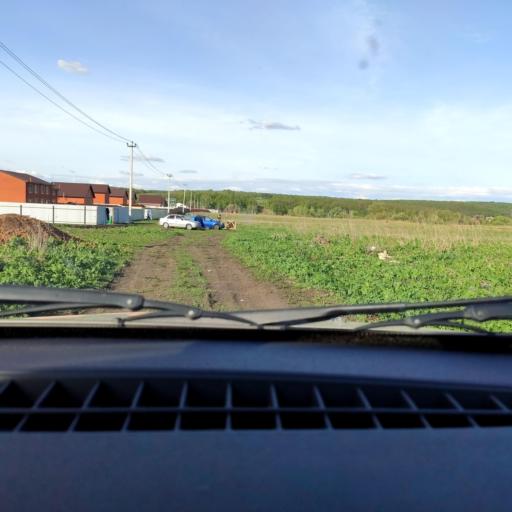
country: RU
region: Bashkortostan
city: Kabakovo
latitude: 54.6799
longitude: 56.1372
